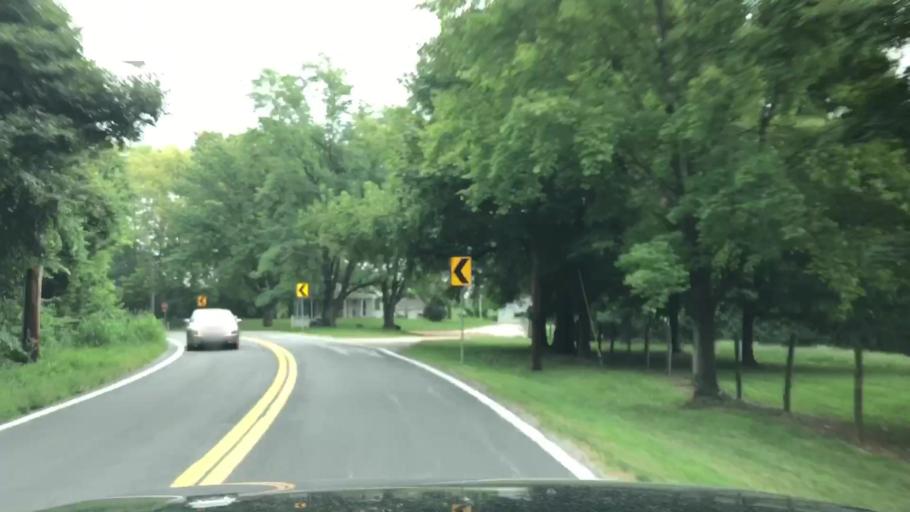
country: US
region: Missouri
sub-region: Saint Louis County
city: Hazelwood
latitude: 38.8142
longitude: -90.3724
